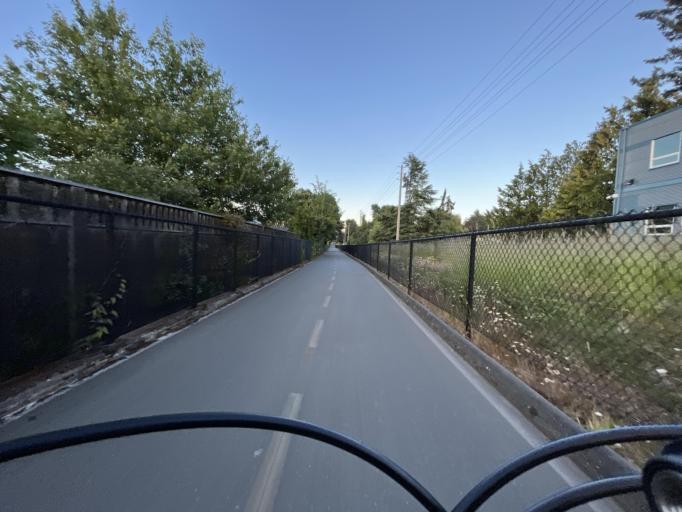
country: CA
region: British Columbia
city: Victoria
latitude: 48.4372
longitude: -123.4166
